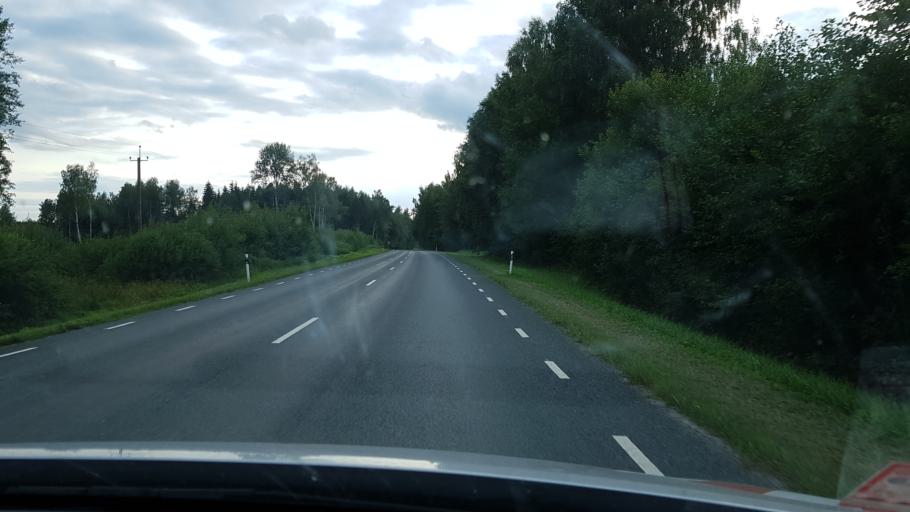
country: EE
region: Vorumaa
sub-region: Antsla vald
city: Vana-Antsla
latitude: 57.9500
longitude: 26.4223
